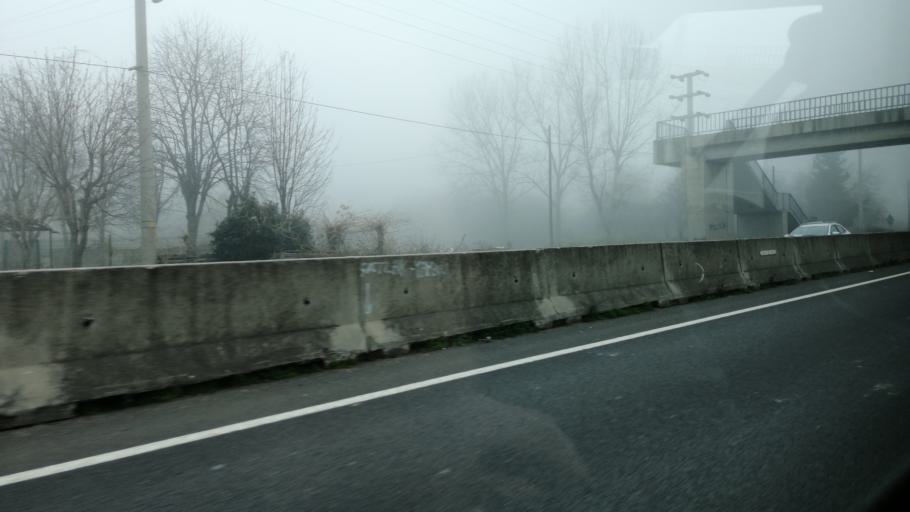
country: TR
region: Yalova
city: Ciftlikkoy
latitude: 40.6768
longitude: 29.3502
